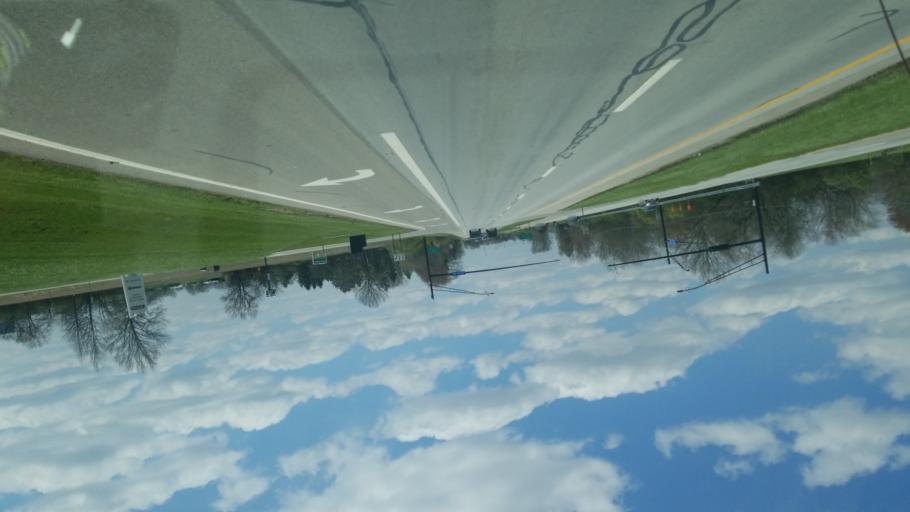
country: US
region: Ohio
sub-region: Delaware County
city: Delaware
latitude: 40.2921
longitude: -83.0287
